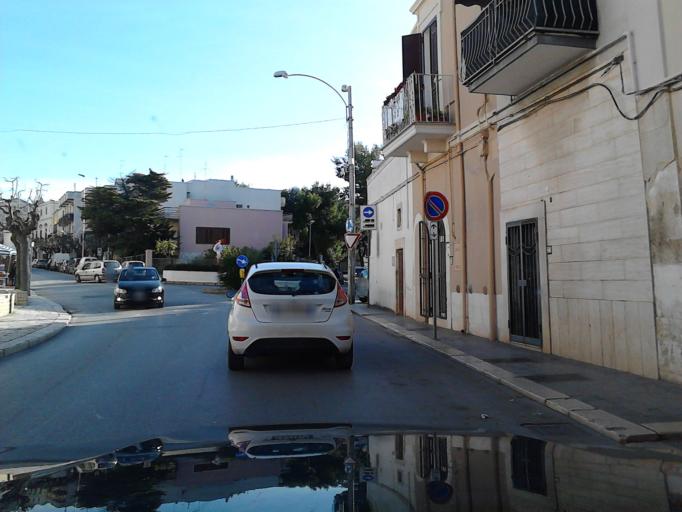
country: IT
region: Apulia
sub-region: Provincia di Bari
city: Rutigliano
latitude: 41.0122
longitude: 17.0026
